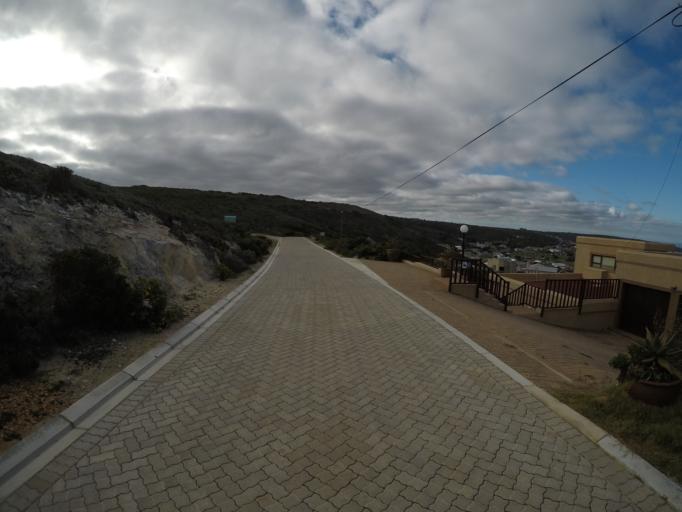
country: ZA
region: Western Cape
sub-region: Eden District Municipality
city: Riversdale
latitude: -34.4298
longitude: 21.3324
